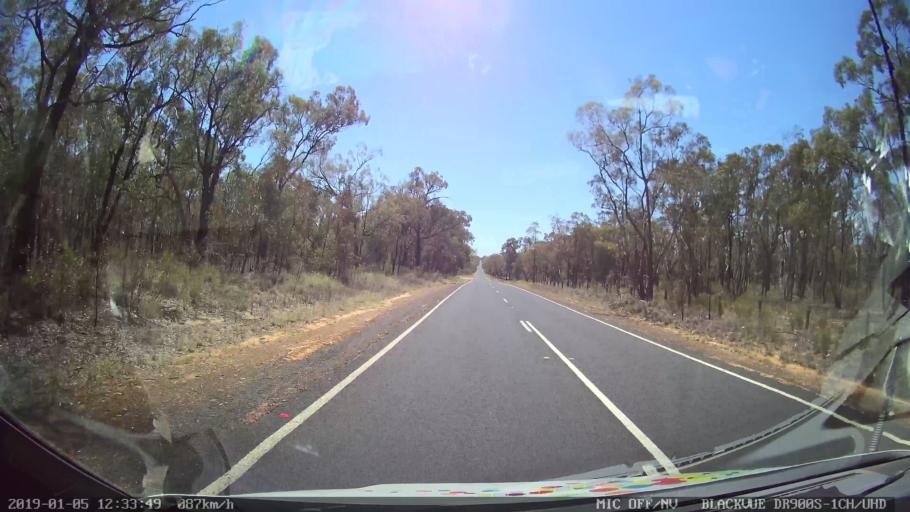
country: AU
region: New South Wales
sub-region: Warrumbungle Shire
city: Coonabarabran
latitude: -31.2137
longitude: 149.4006
